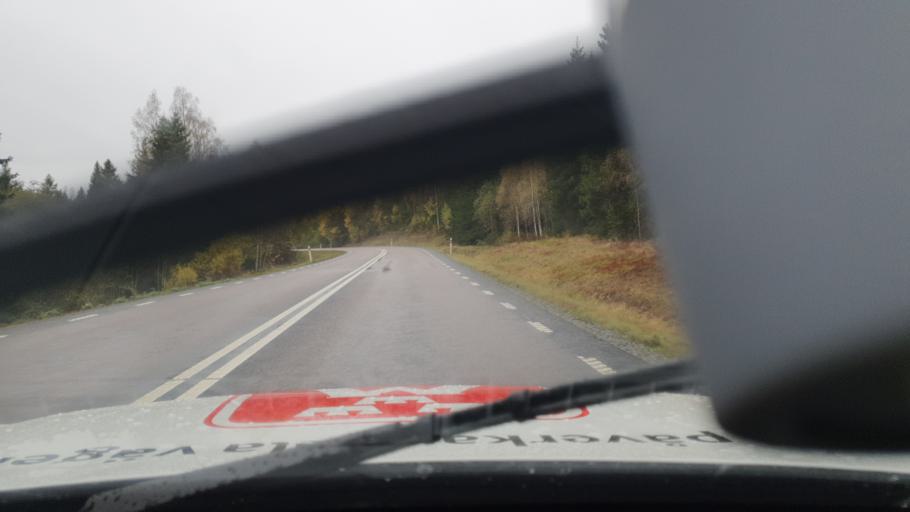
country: SE
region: Vaestra Goetaland
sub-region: Dals-Ed Kommun
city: Ed
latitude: 58.9088
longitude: 12.0039
